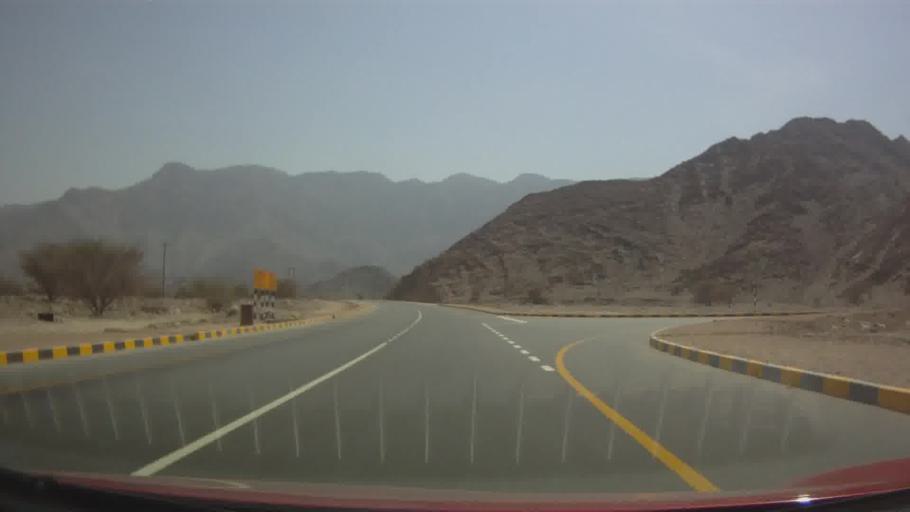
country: OM
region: Muhafazat Masqat
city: Muscat
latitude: 23.4105
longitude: 58.7800
